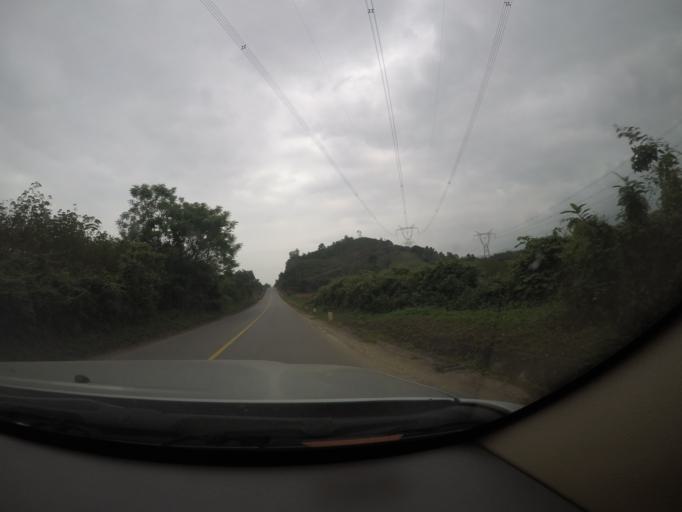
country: VN
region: Quang Binh
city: Hoan Lao
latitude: 17.6005
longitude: 106.4158
